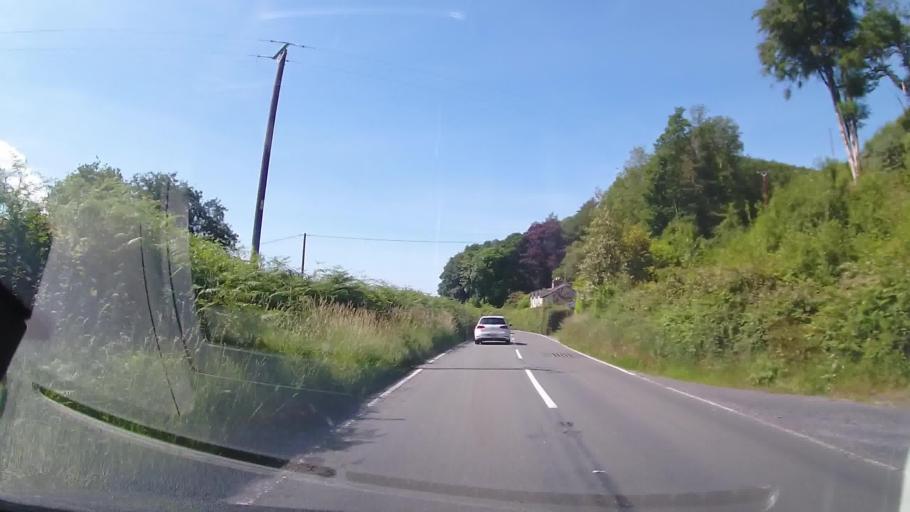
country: GB
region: Wales
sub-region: Sir Powys
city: Machynlleth
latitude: 52.5705
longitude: -3.9534
